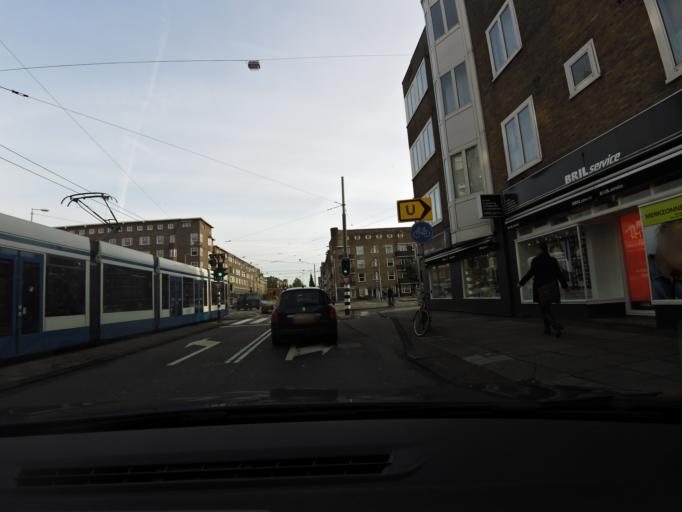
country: NL
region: North Holland
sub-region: Gemeente Amsterdam
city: Amsterdam
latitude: 52.3459
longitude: 4.9055
